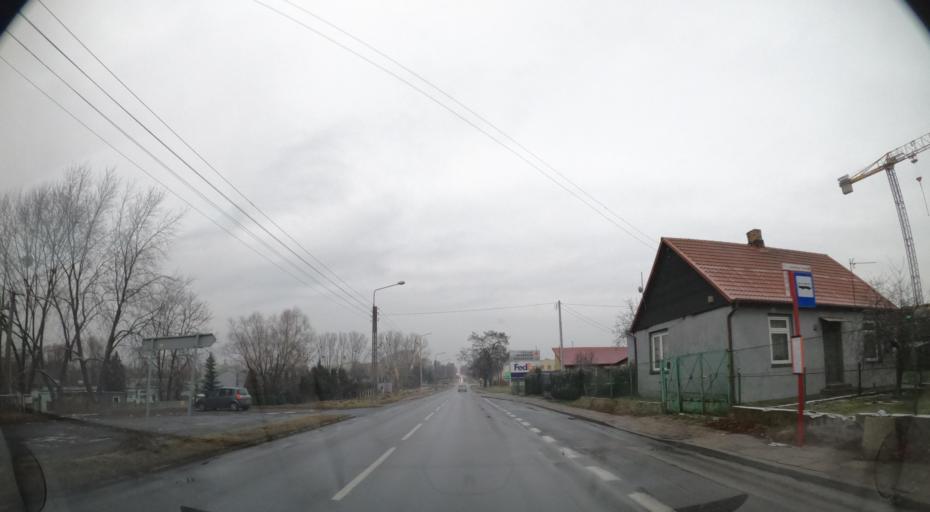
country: PL
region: Masovian Voivodeship
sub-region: Powiat radomski
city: Trablice
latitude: 51.3820
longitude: 21.1204
